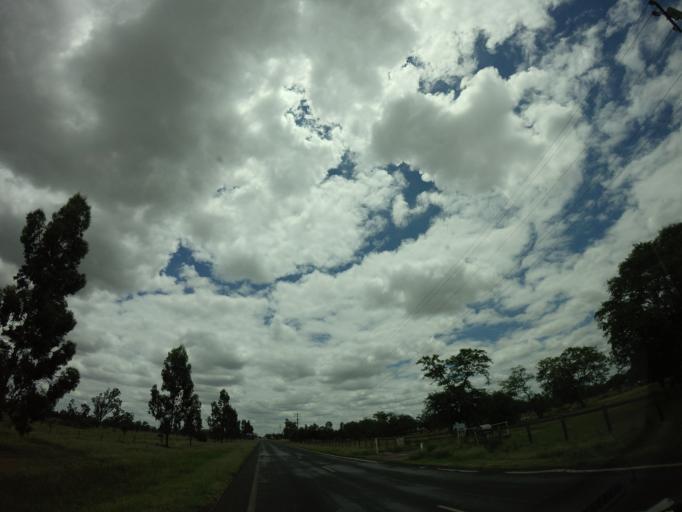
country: AU
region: Queensland
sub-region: Goondiwindi
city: Goondiwindi
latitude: -28.5158
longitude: 150.2888
